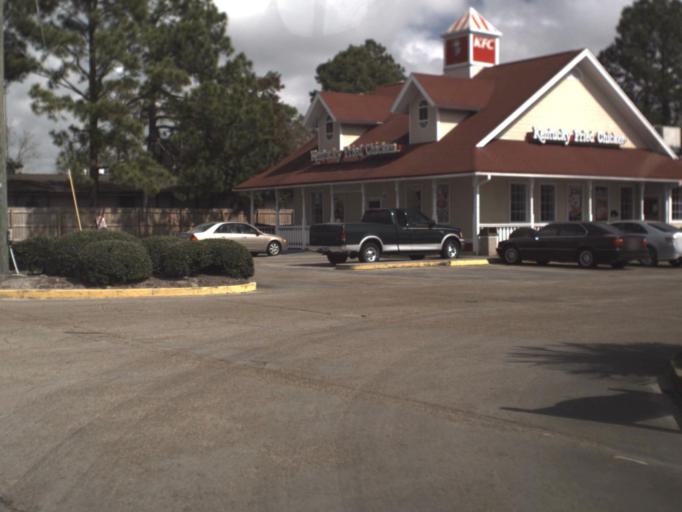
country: US
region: Florida
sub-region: Bay County
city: Parker
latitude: 30.1395
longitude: -85.5911
